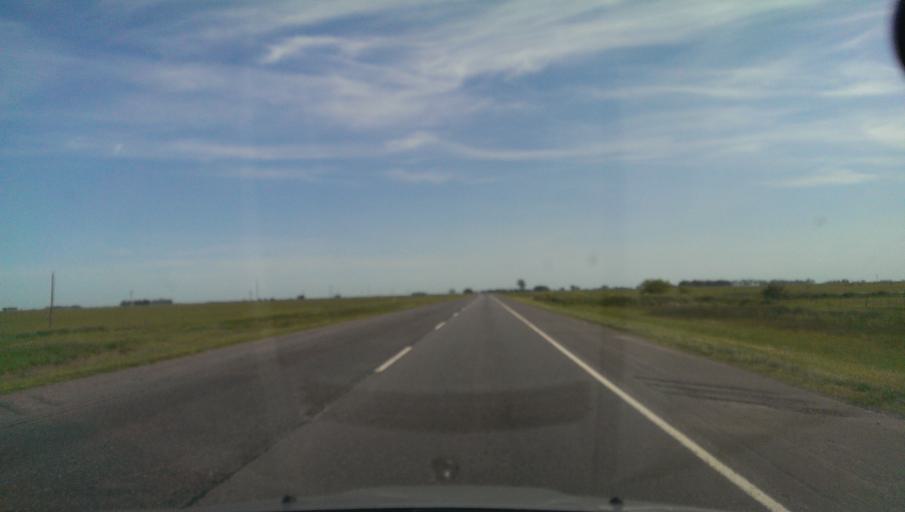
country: AR
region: Buenos Aires
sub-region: Partido de Azul
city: Azul
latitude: -36.3967
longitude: -59.5025
